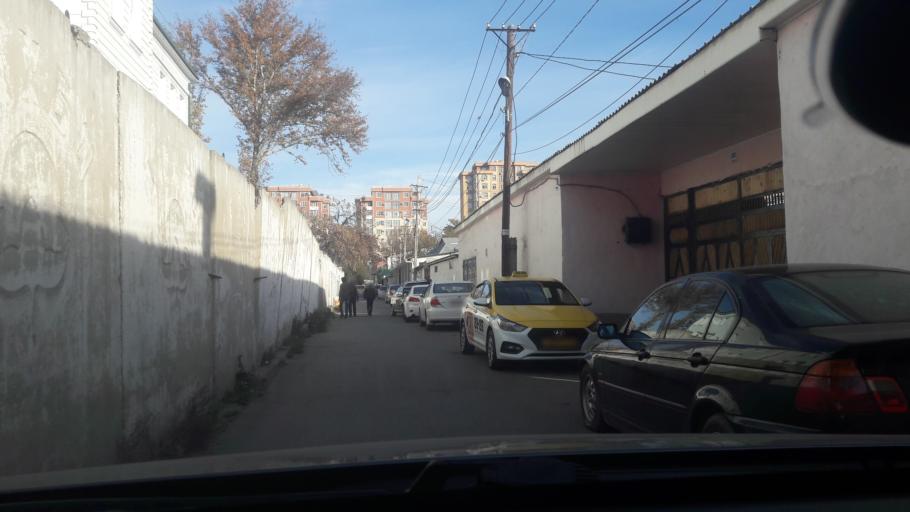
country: TJ
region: Dushanbe
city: Dushanbe
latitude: 38.5821
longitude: 68.7595
